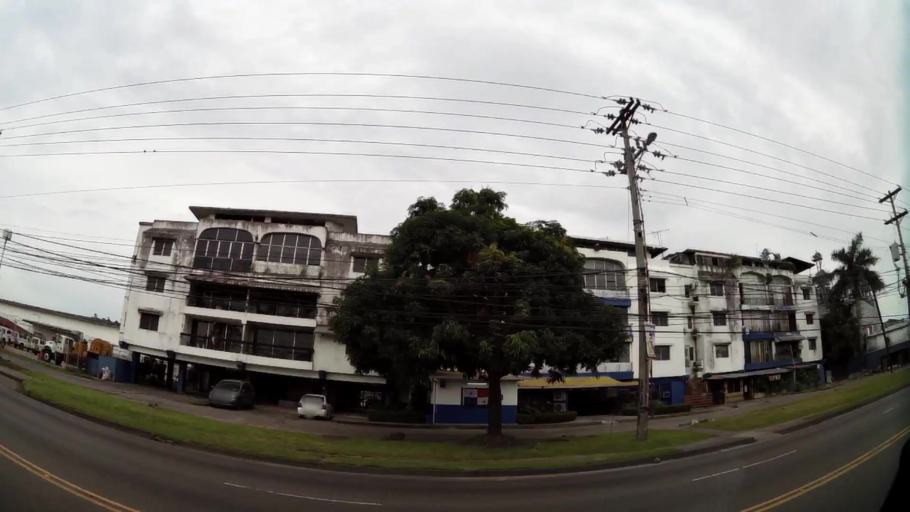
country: PA
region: Panama
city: San Miguelito
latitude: 9.0366
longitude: -79.4708
